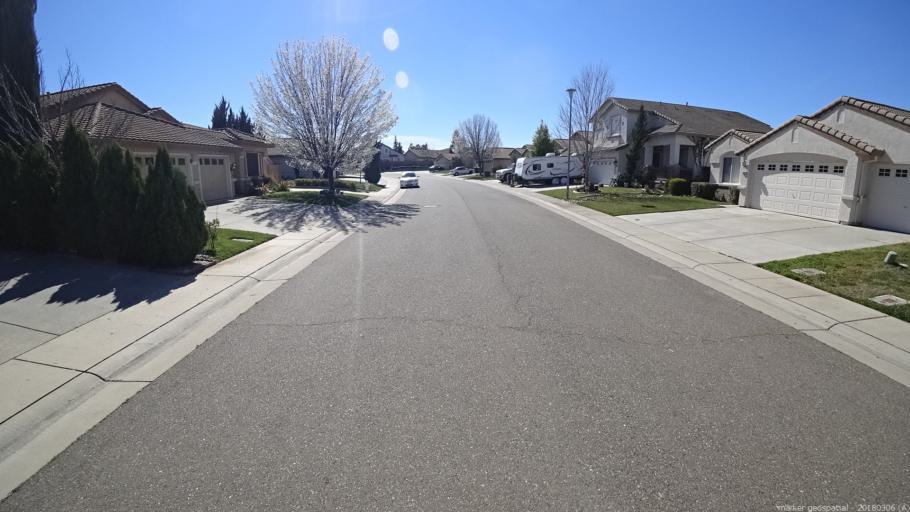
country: US
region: California
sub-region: Sacramento County
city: Vineyard
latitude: 38.4686
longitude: -121.3560
